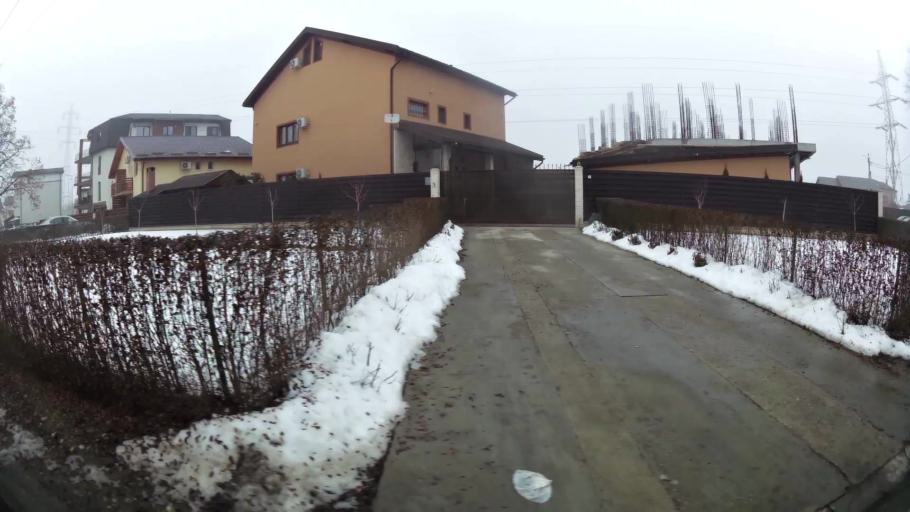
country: RO
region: Ilfov
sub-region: Comuna Chiajna
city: Rosu
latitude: 44.4457
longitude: 26.0036
